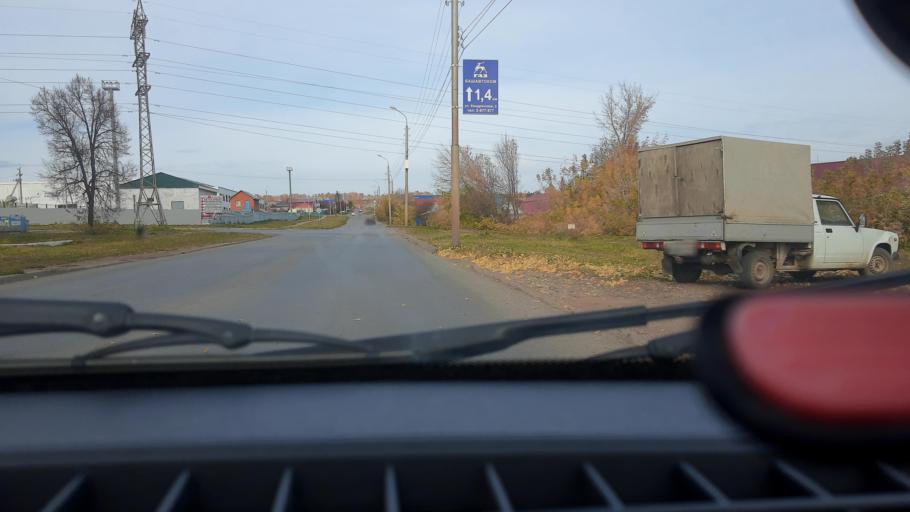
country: RU
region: Bashkortostan
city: Avdon
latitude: 54.6876
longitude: 55.8096
